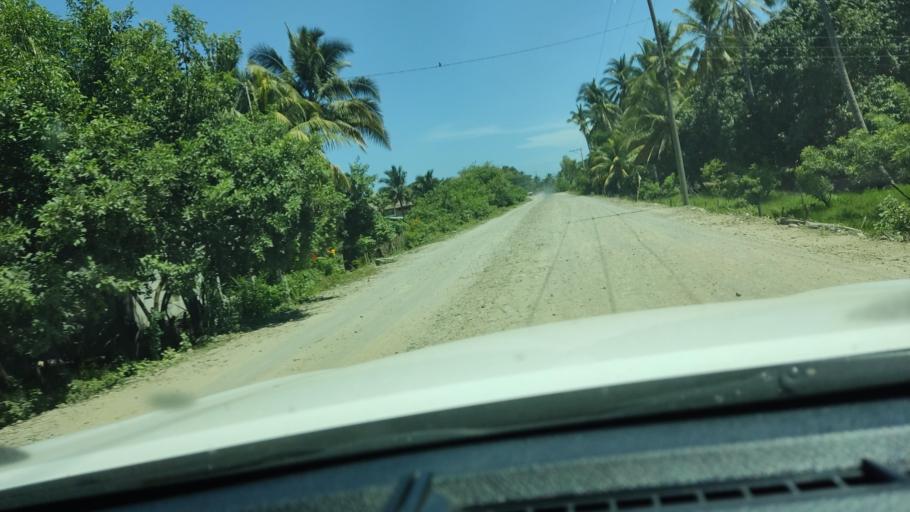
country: SV
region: Ahuachapan
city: San Francisco Menendez
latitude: 13.7673
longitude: -90.1152
